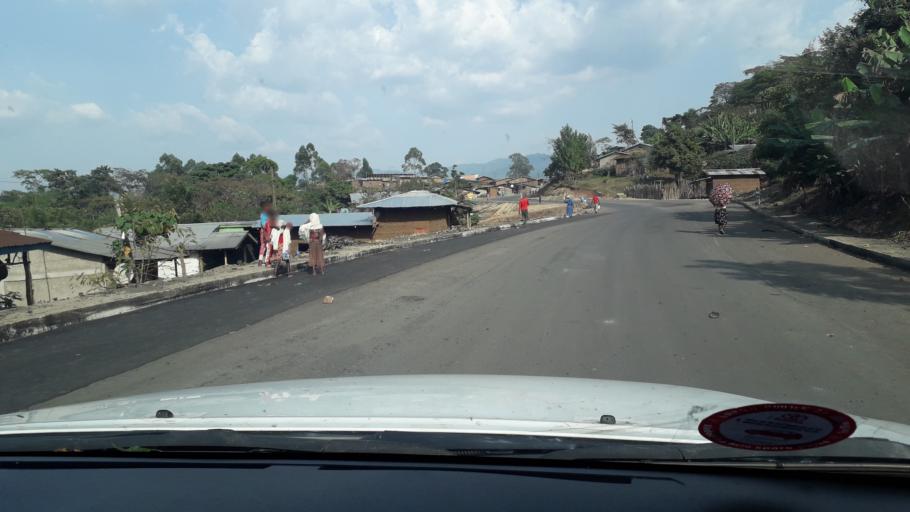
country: ET
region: Southern Nations, Nationalities, and People's Region
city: Mizan Teferi
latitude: 6.9337
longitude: 35.4940
